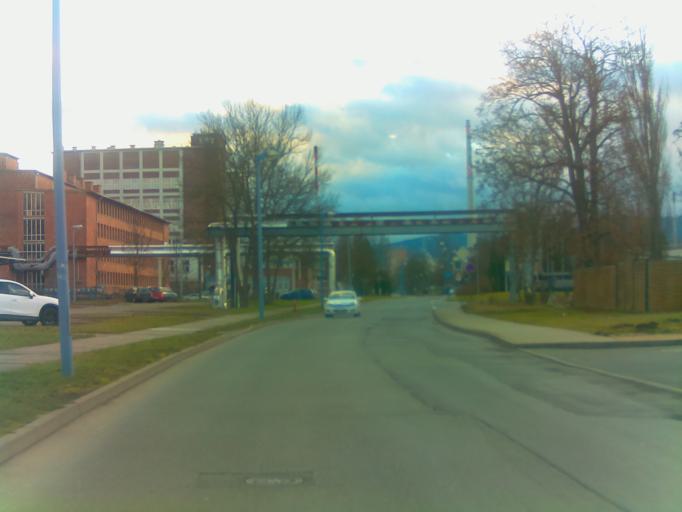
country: DE
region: Thuringia
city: Rudolstadt
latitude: 50.6950
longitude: 11.3296
